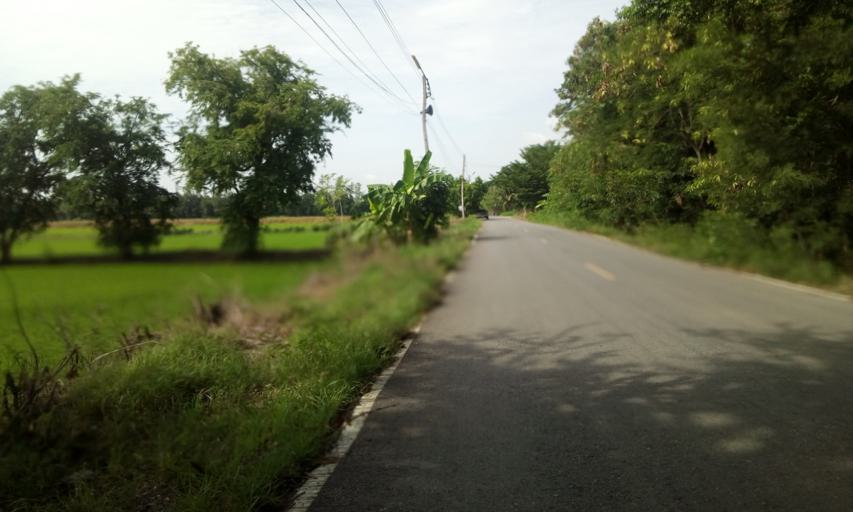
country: TH
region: Pathum Thani
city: Ban Lam Luk Ka
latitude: 14.0123
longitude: 100.8459
